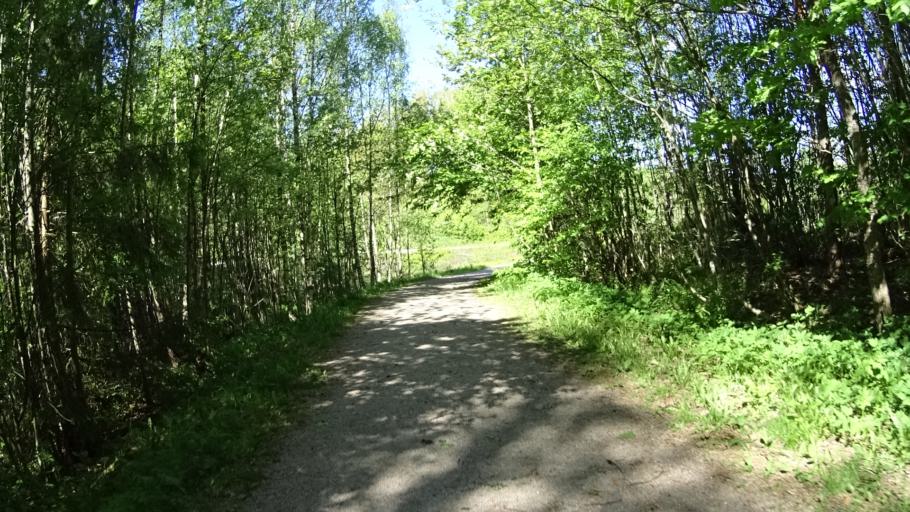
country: FI
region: Uusimaa
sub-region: Helsinki
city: Espoo
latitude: 60.2136
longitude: 24.6223
